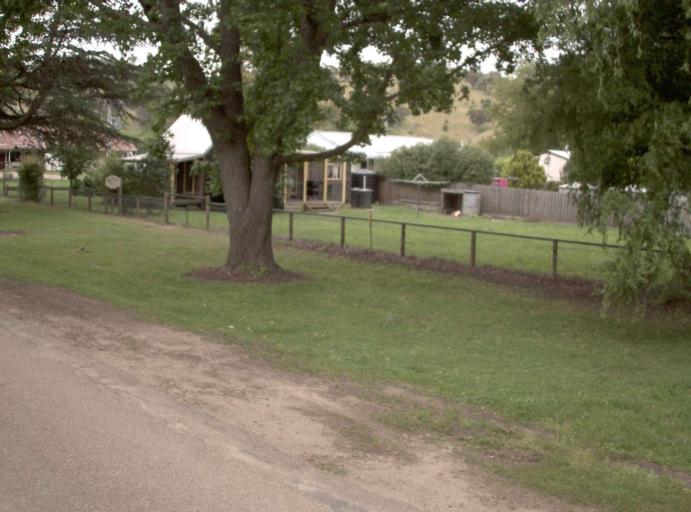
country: AU
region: Victoria
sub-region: East Gippsland
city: Bairnsdale
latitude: -37.4627
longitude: 147.2507
